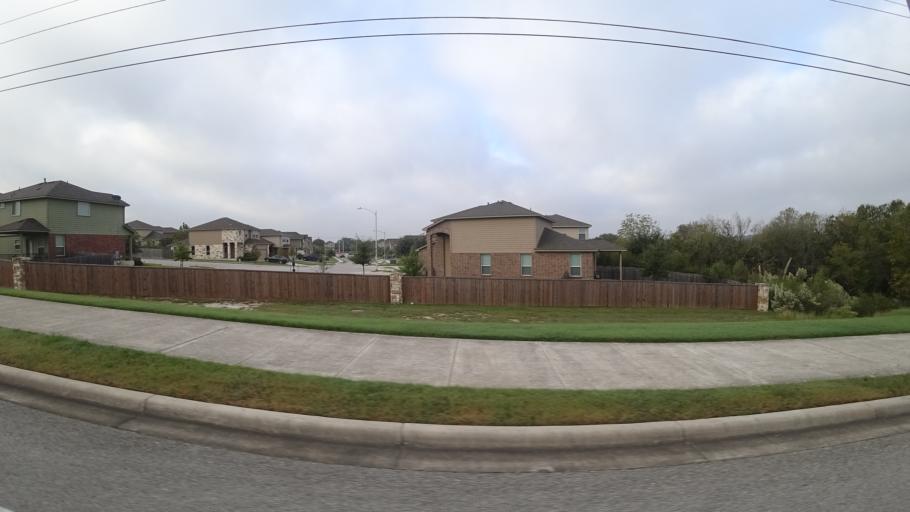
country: US
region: Texas
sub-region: Travis County
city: Pflugerville
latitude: 30.3692
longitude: -97.6531
